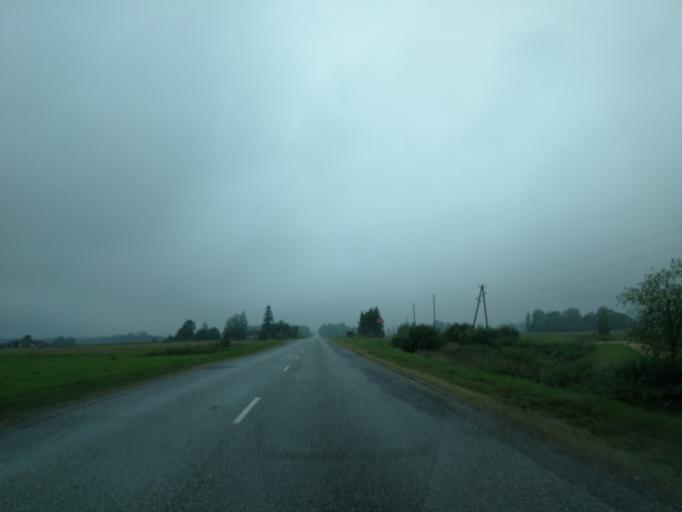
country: LV
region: Varkava
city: Vecvarkava
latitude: 56.3088
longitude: 26.5777
